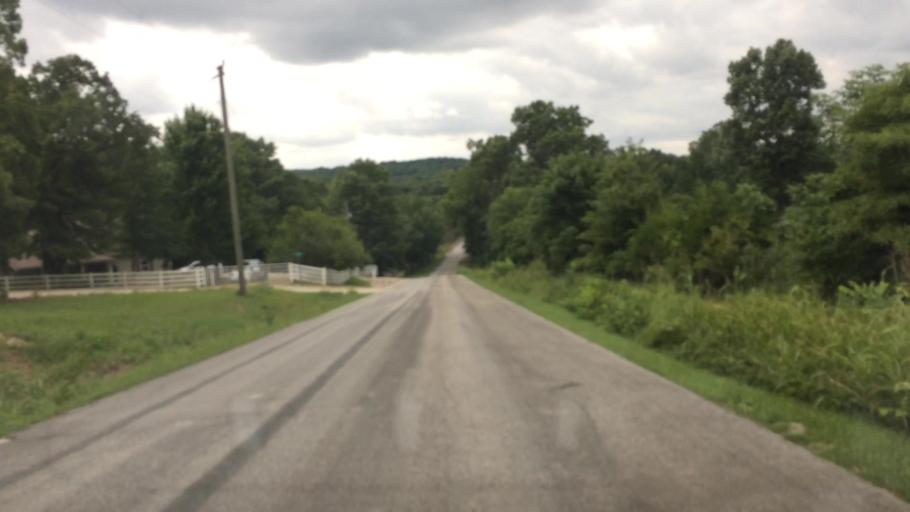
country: US
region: Missouri
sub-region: Webster County
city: Marshfield
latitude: 37.3071
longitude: -92.9846
